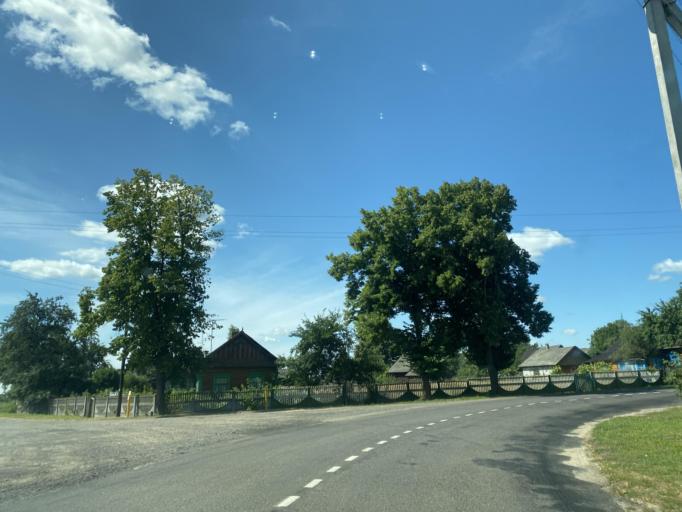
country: BY
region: Brest
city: Ivanava
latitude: 52.2316
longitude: 25.6623
